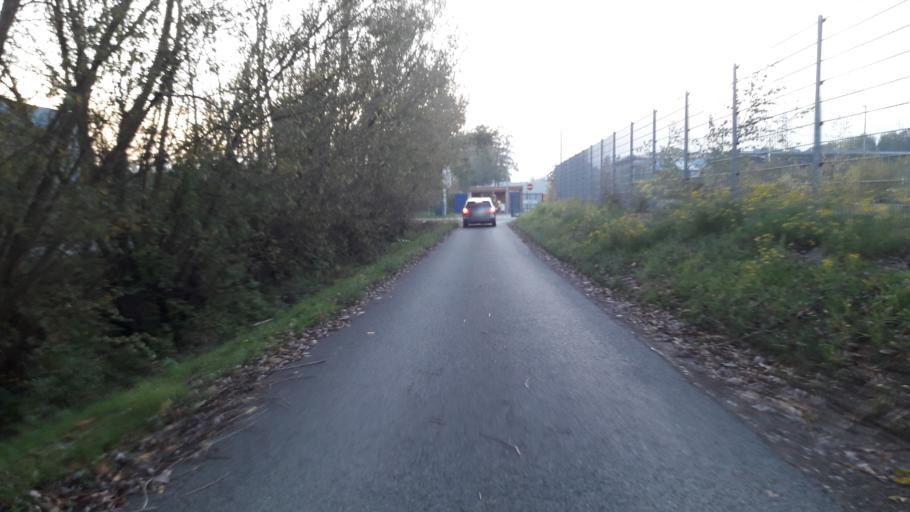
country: DE
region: North Rhine-Westphalia
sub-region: Regierungsbezirk Detmold
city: Paderborn
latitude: 51.7492
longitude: 8.7517
